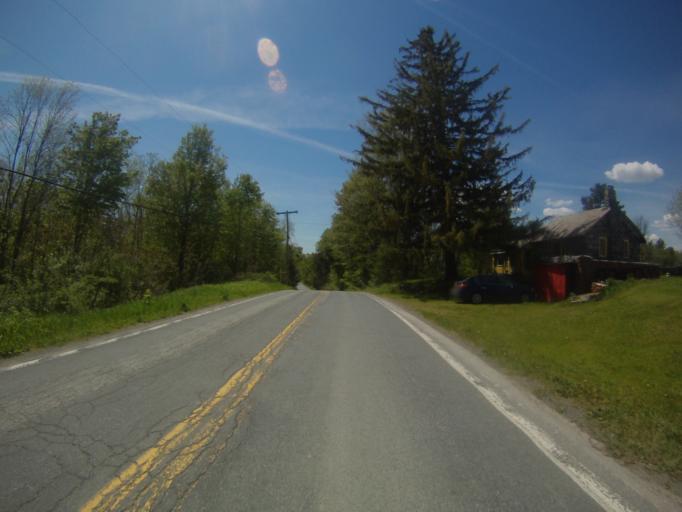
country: US
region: New York
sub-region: Essex County
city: Port Henry
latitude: 43.9760
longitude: -73.4224
